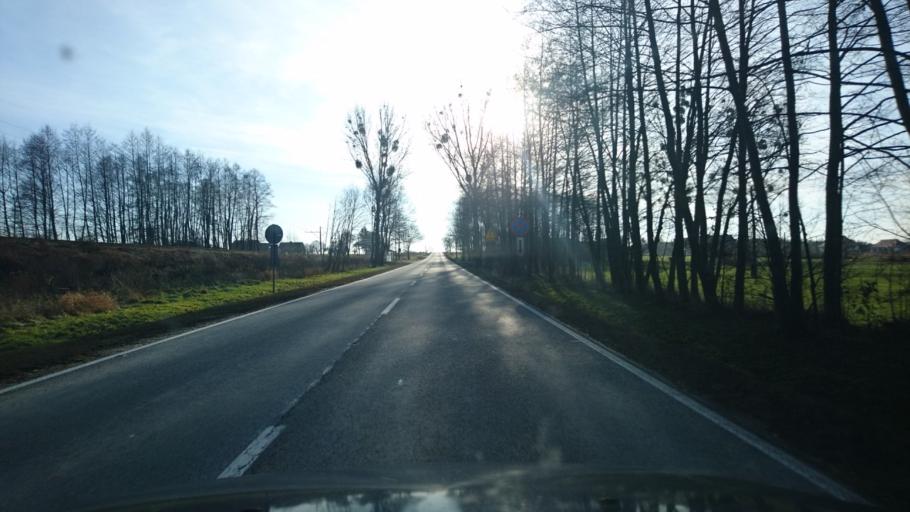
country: PL
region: Opole Voivodeship
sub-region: Powiat oleski
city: Dalachow
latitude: 51.0668
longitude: 18.6010
